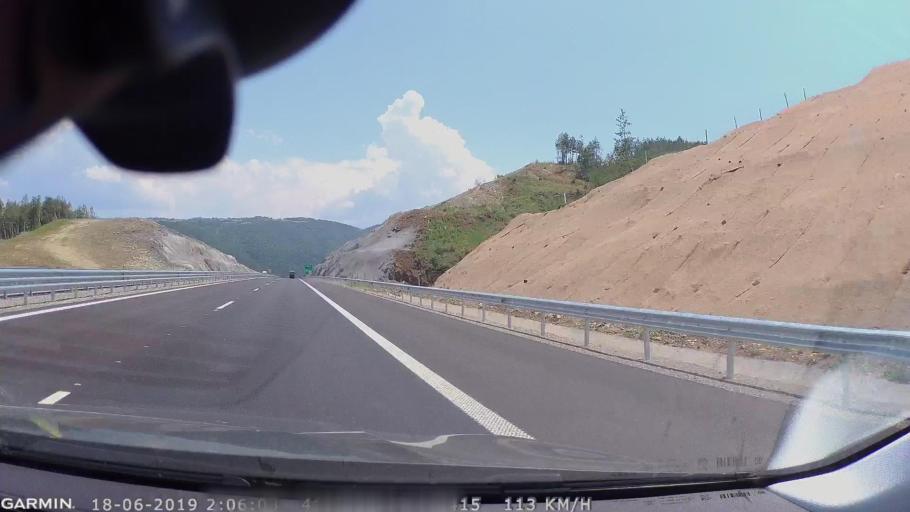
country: BG
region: Blagoevgrad
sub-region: Obshtina Blagoevgrad
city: Blagoevgrad
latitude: 41.9702
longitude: 23.0850
